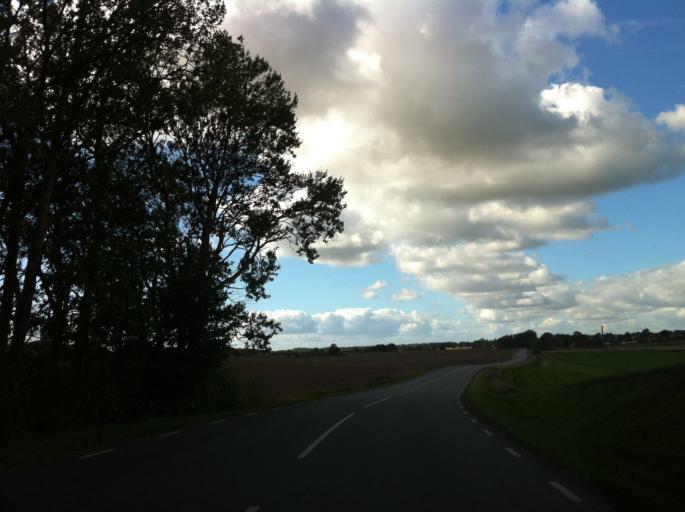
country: SE
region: Skane
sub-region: Tomelilla Kommun
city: Tomelilla
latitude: 55.6440
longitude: 13.9864
